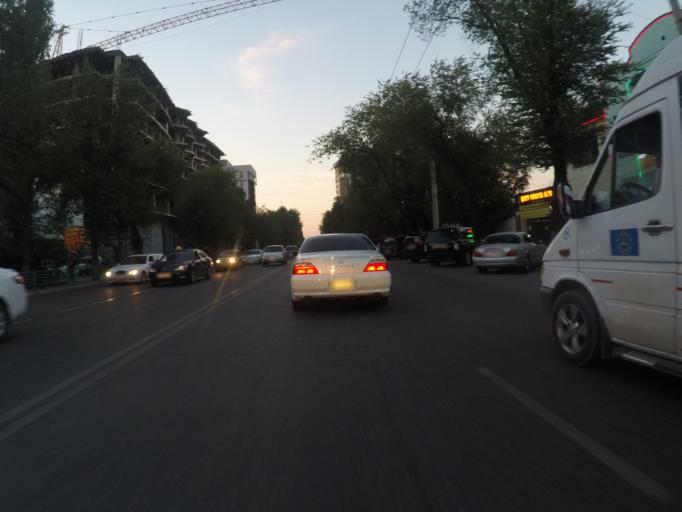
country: KG
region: Chuy
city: Bishkek
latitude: 42.8529
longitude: 74.6099
